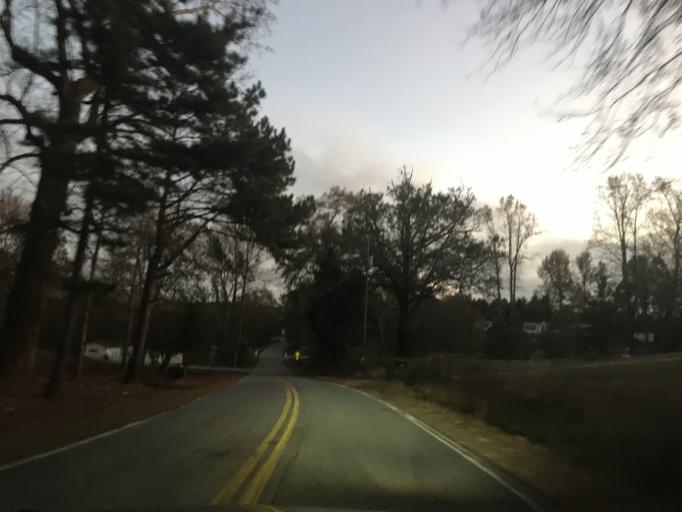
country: US
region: South Carolina
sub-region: Spartanburg County
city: Mayo
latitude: 35.0827
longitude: -81.9007
